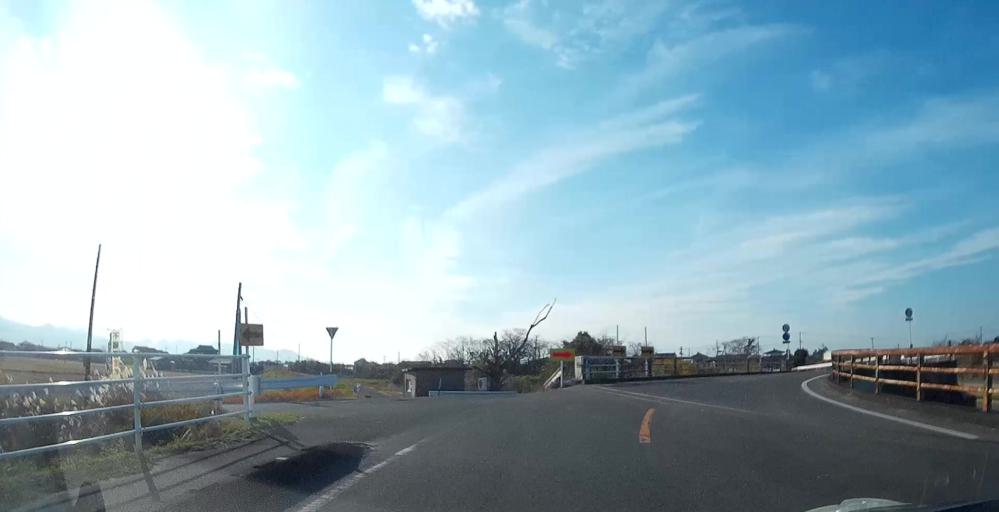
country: JP
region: Kumamoto
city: Uto
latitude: 32.7328
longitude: 130.6525
